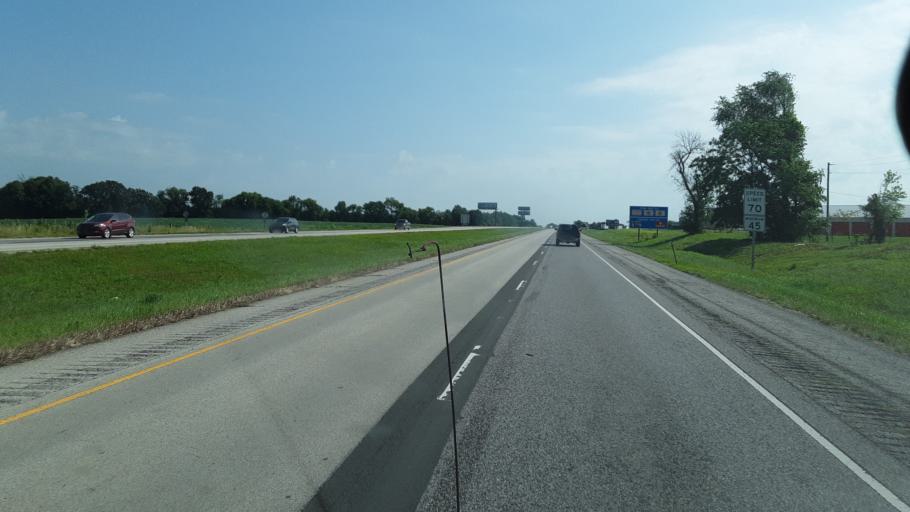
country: US
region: Illinois
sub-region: Fayette County
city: Vandalia
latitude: 38.9740
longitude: -89.1244
